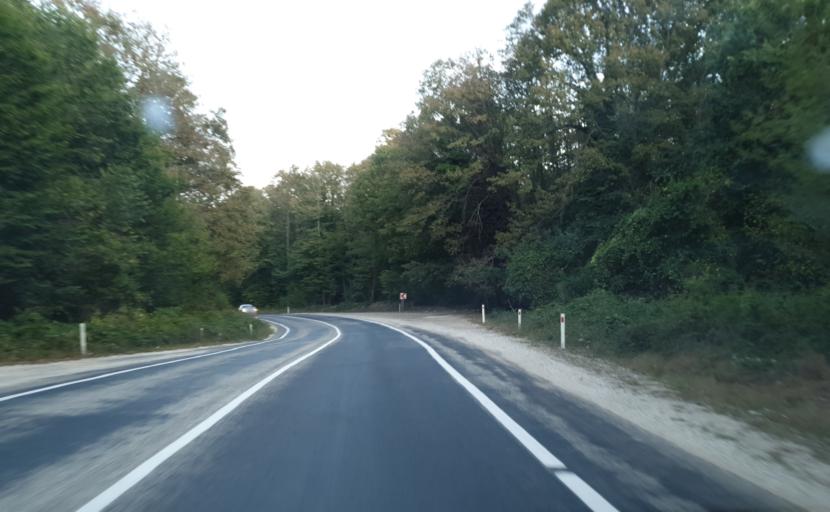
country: TR
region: Kirklareli
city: Igneada
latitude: 41.8801
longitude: 27.9014
